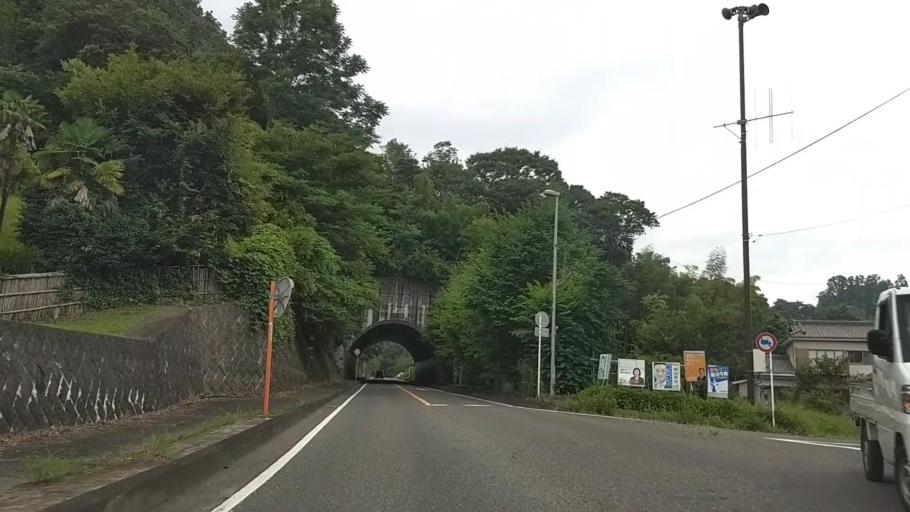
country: JP
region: Kanagawa
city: Hadano
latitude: 35.3372
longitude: 139.1978
